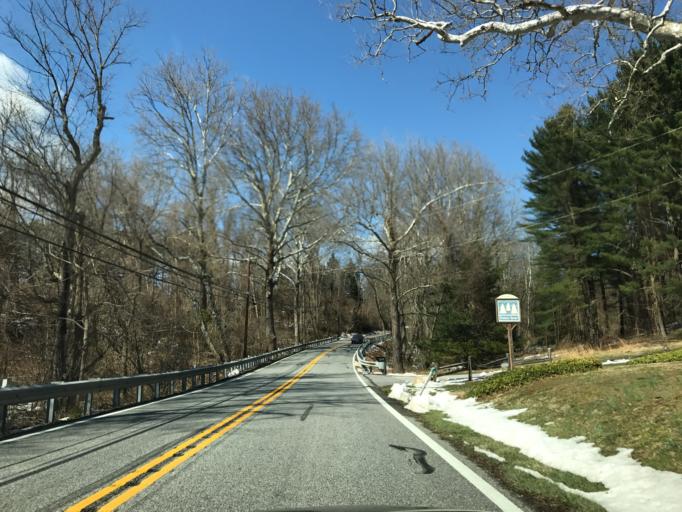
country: US
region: Maryland
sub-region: Carroll County
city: Hampstead
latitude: 39.5580
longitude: -76.7462
